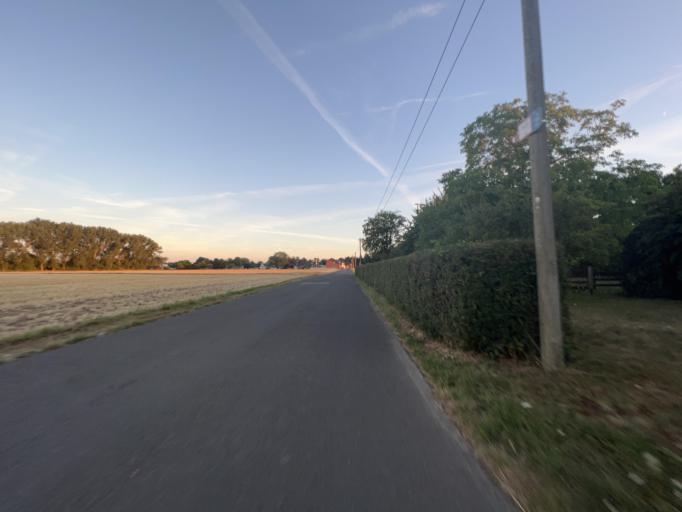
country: DE
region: North Rhine-Westphalia
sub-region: Regierungsbezirk Koln
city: Langerwehe
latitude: 50.8144
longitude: 6.4197
